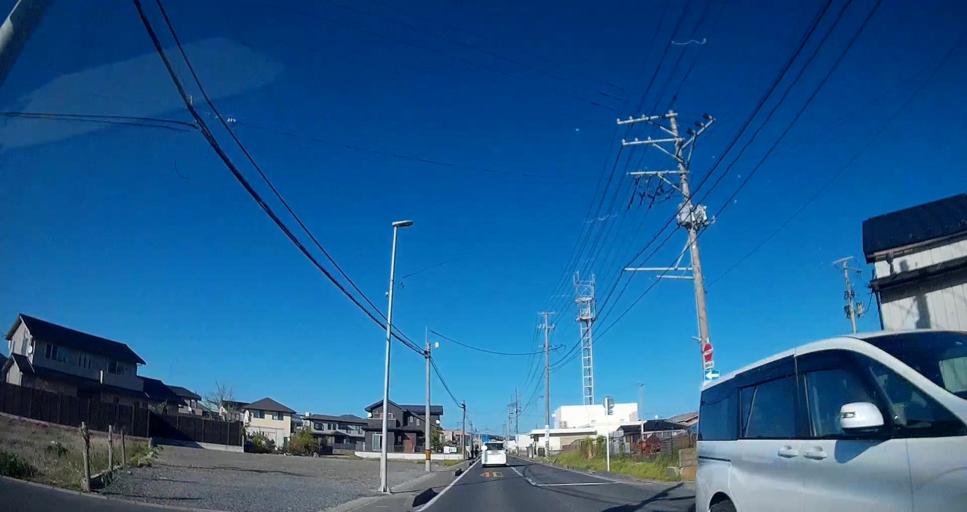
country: JP
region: Miyagi
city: Ishinomaki
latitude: 38.4168
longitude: 141.3627
